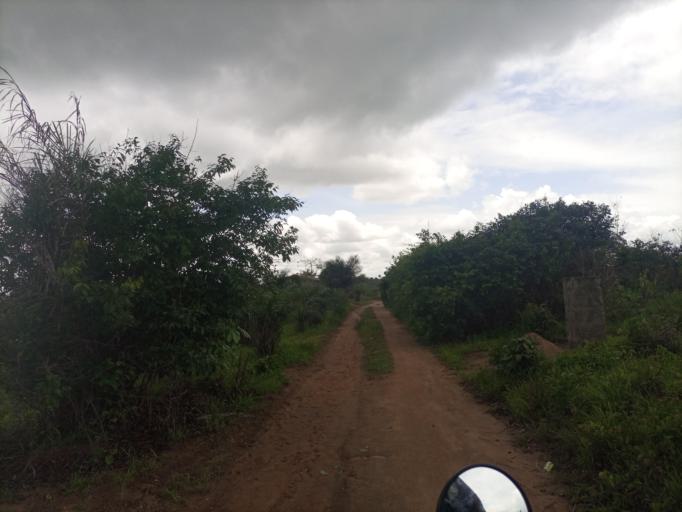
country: SL
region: Northern Province
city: Masoyila
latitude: 8.5785
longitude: -13.1568
